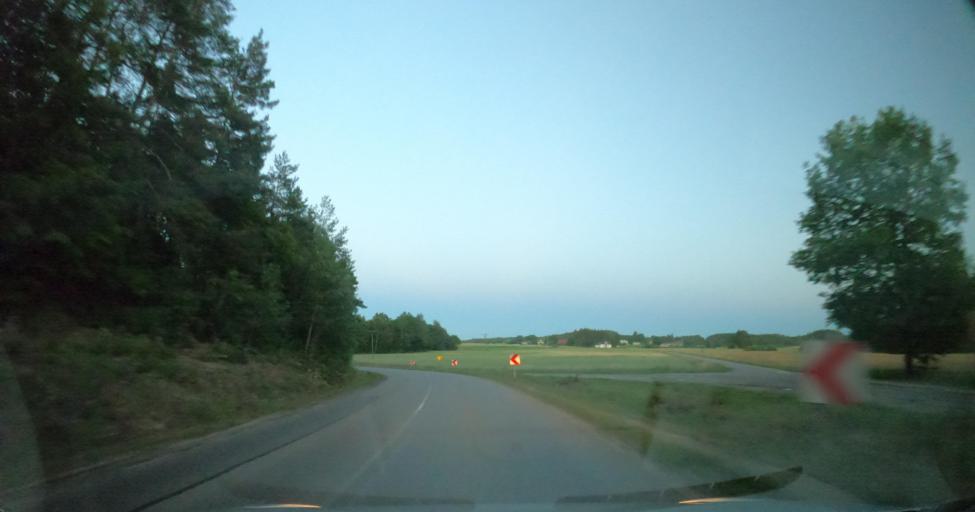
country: PL
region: Pomeranian Voivodeship
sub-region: Powiat wejherowski
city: Szemud
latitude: 54.4669
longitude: 18.2822
